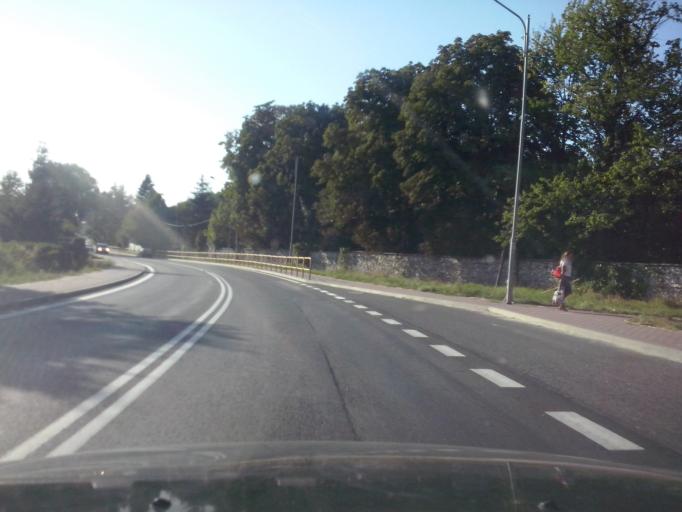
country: PL
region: Swietokrzyskie
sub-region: Powiat kielecki
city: Pierzchnica
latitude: 50.6682
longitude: 20.6745
